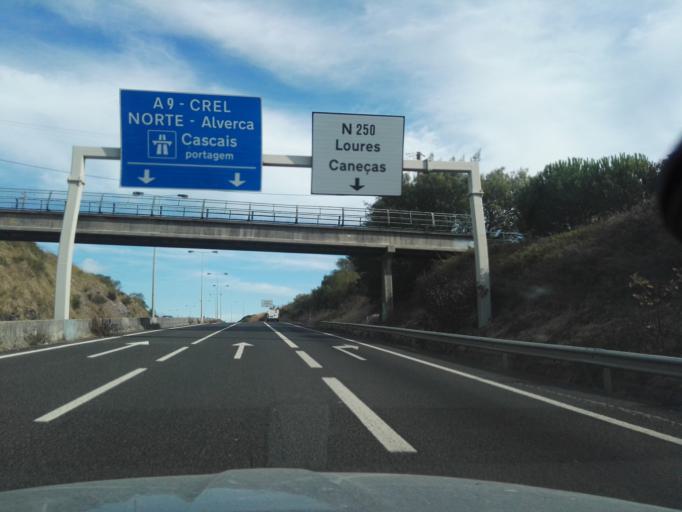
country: PT
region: Lisbon
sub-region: Odivelas
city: Ramada
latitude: 38.8110
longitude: -9.1833
